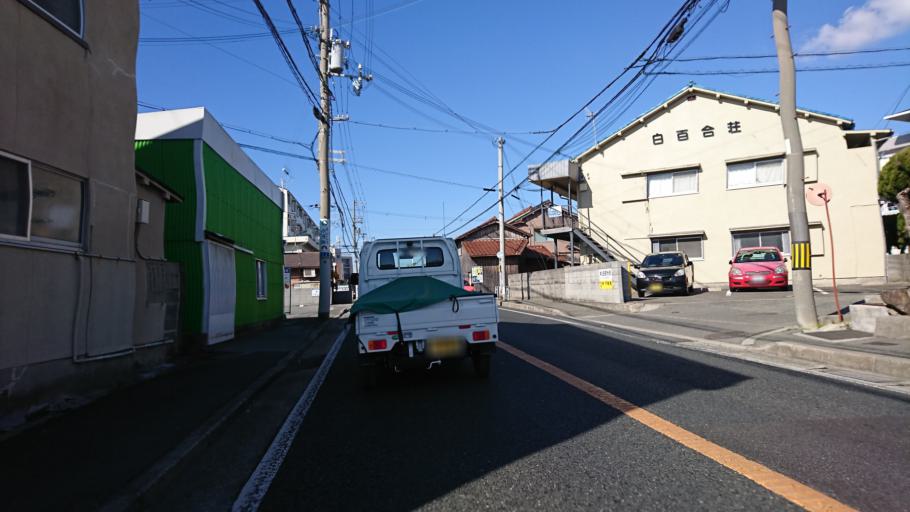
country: JP
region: Hyogo
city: Akashi
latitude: 34.6511
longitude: 134.9654
